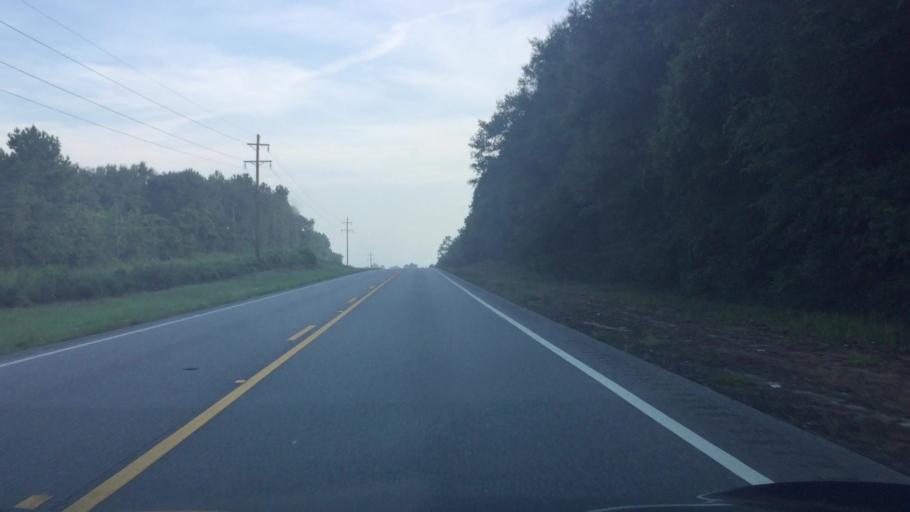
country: US
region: Alabama
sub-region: Covington County
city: Florala
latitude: 31.0678
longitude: -86.4014
